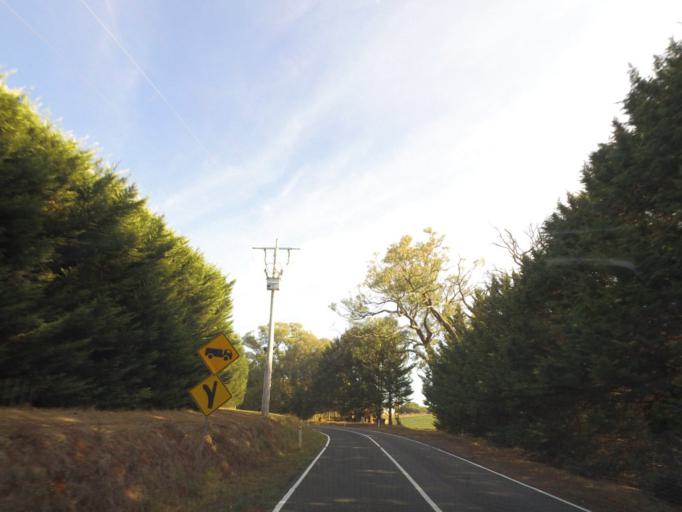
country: AU
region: Victoria
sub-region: Yarra Ranges
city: Mount Evelyn
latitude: -37.8094
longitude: 145.4447
